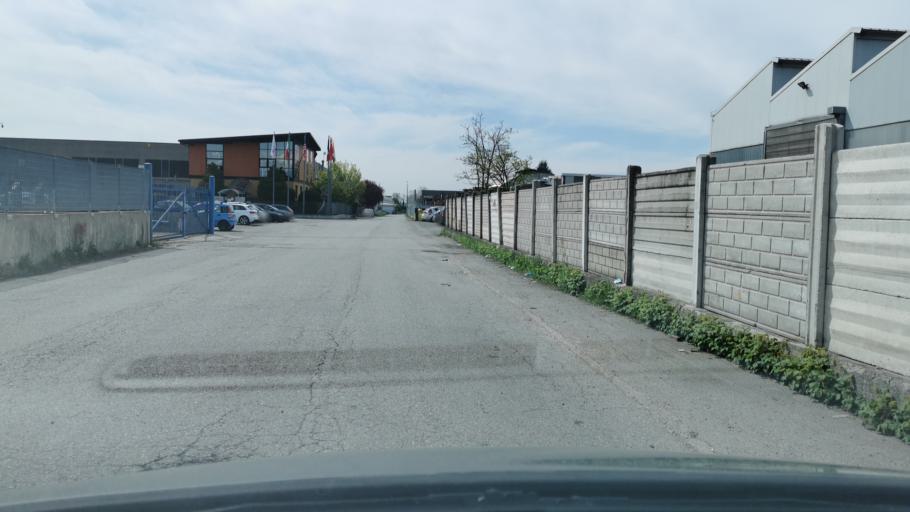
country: IT
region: Piedmont
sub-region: Provincia di Torino
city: Busano
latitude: 45.3313
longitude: 7.6700
